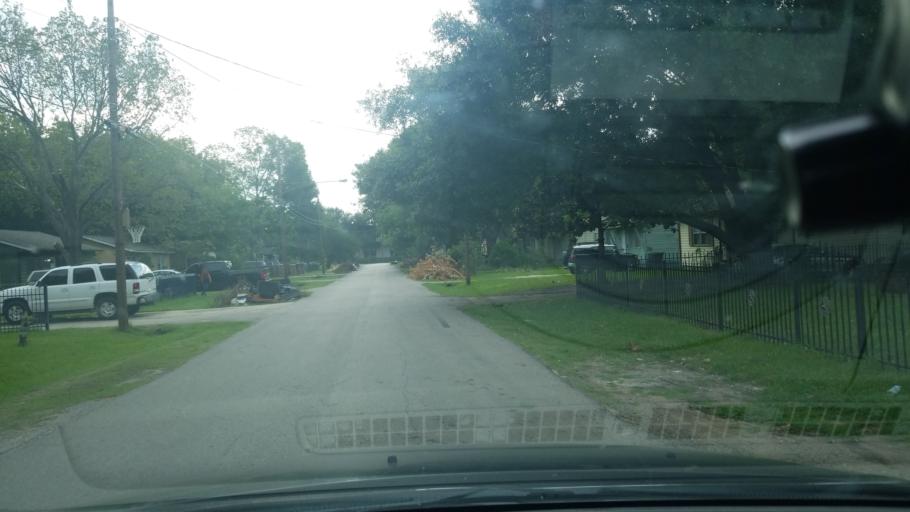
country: US
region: Texas
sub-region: Dallas County
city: Balch Springs
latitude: 32.7325
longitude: -96.6680
